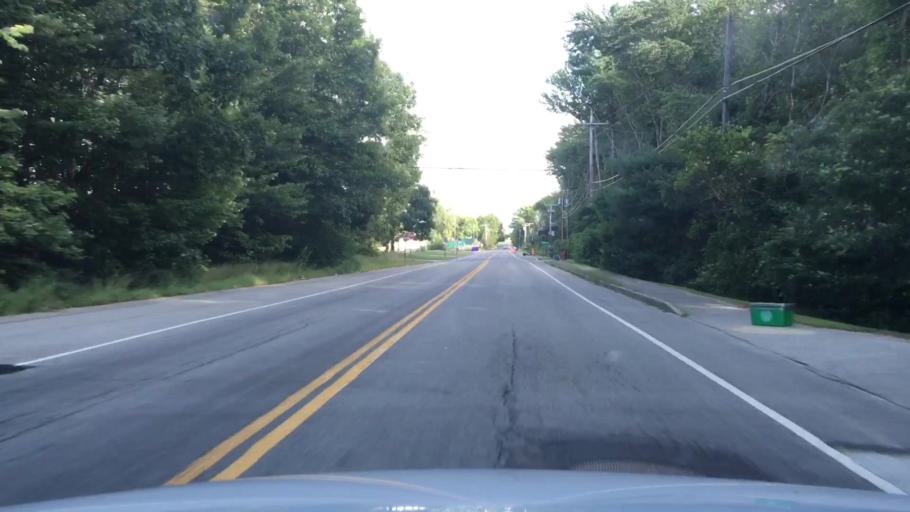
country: US
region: Maine
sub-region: York County
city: Eliot
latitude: 43.1262
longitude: -70.8385
